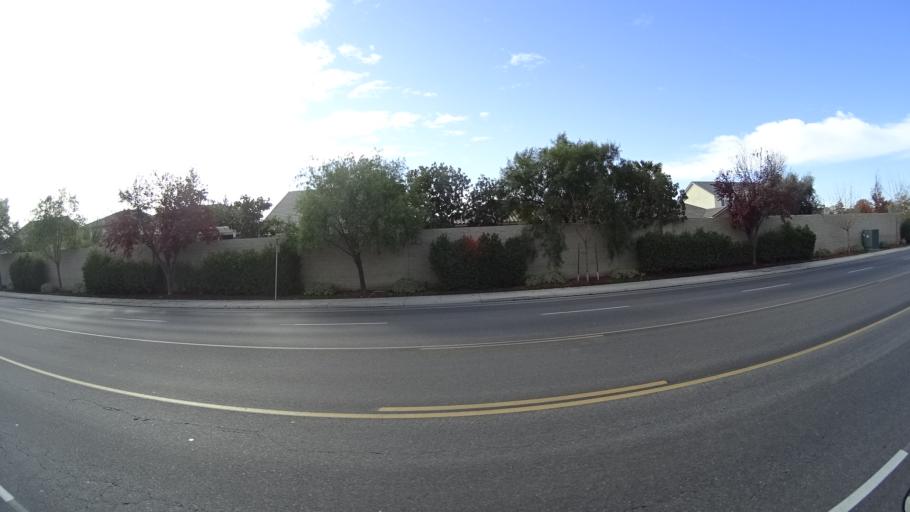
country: US
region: California
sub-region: Kern County
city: Greenacres
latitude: 35.3035
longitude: -119.1159
